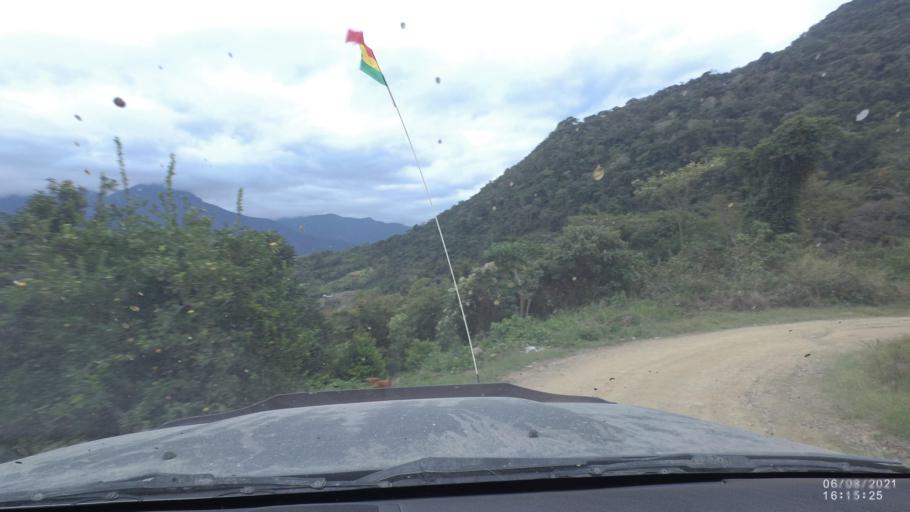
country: BO
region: La Paz
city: Quime
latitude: -16.5522
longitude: -66.7377
